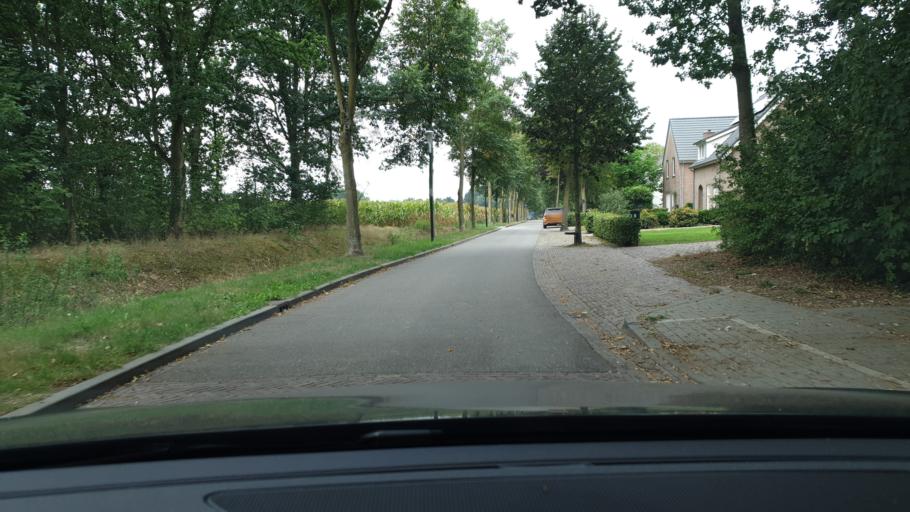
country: NL
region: North Brabant
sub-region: Gemeente Bladel en Netersel
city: Bladel
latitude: 51.3668
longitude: 5.2481
